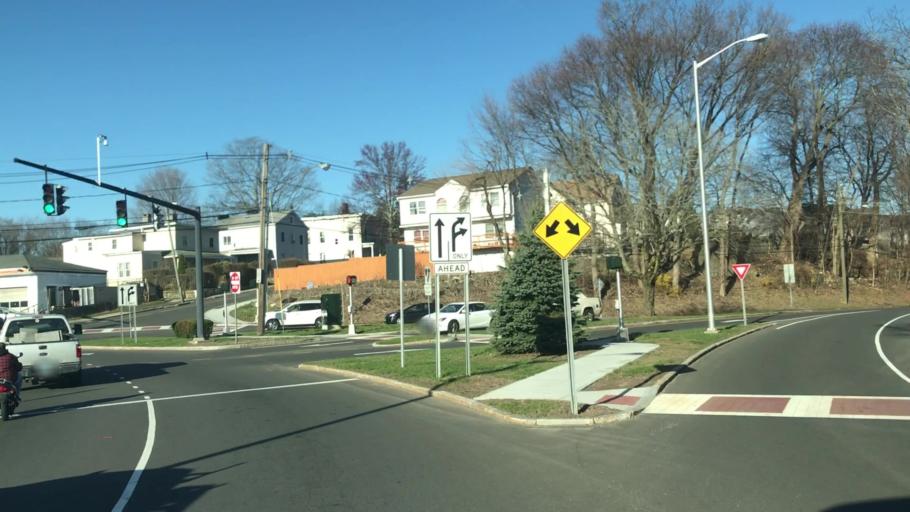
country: US
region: Connecticut
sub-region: Fairfield County
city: Danbury
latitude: 41.3961
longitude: -73.4568
